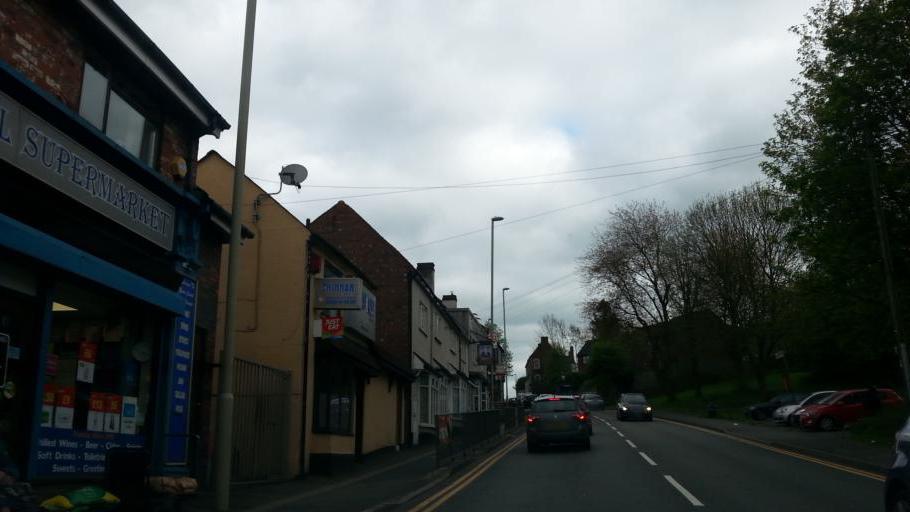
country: GB
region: England
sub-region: Sandwell
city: Cradley Heath
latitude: 52.4591
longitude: -2.0845
